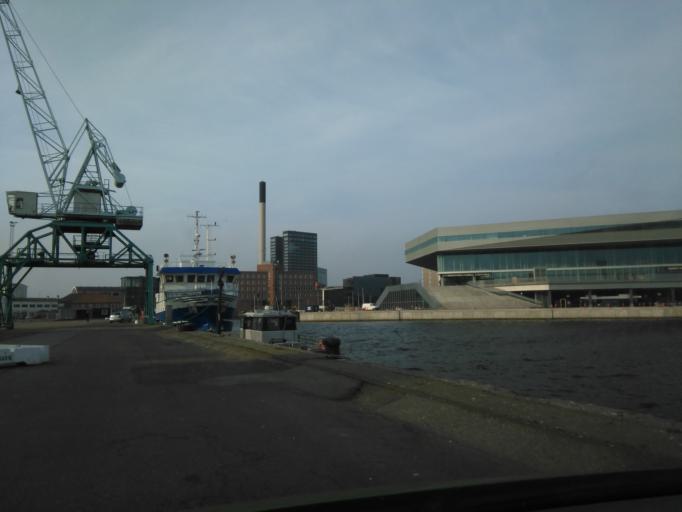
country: DK
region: Central Jutland
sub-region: Arhus Kommune
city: Arhus
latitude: 56.1538
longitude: 10.2176
